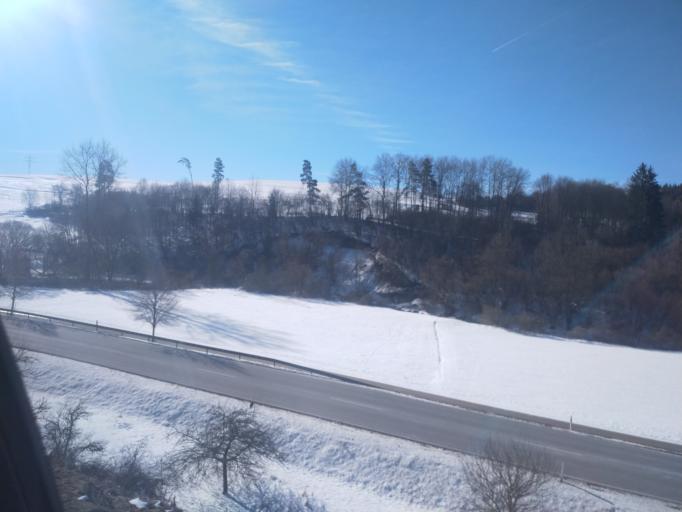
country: DE
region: Baden-Wuerttemberg
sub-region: Freiburg Region
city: Aldingen
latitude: 48.1180
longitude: 8.6855
